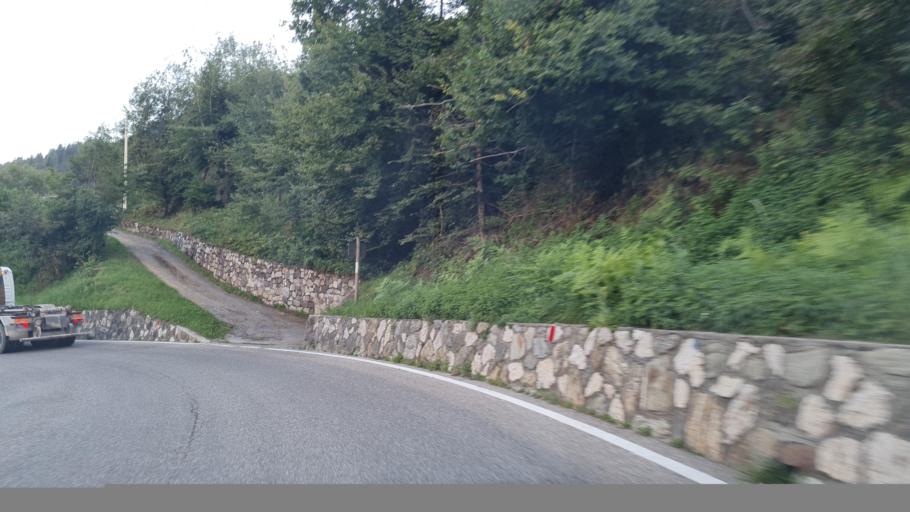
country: IT
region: Trentino-Alto Adige
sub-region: Provincia di Trento
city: Siror
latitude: 46.2279
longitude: 11.8085
